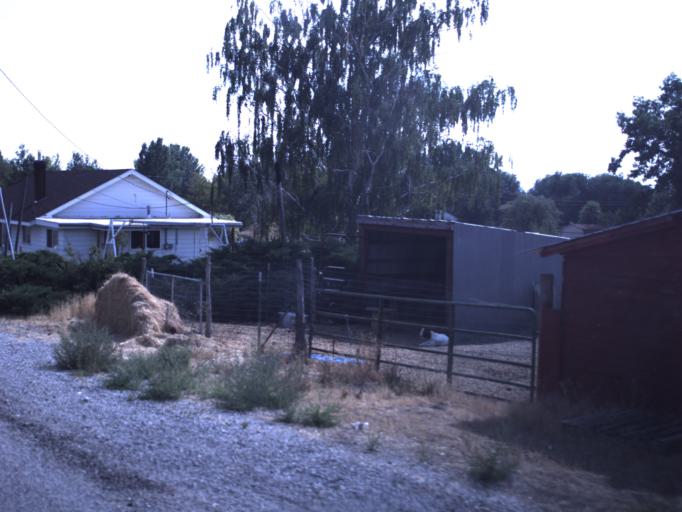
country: US
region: Utah
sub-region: Box Elder County
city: Honeyville
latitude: 41.6395
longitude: -112.0796
